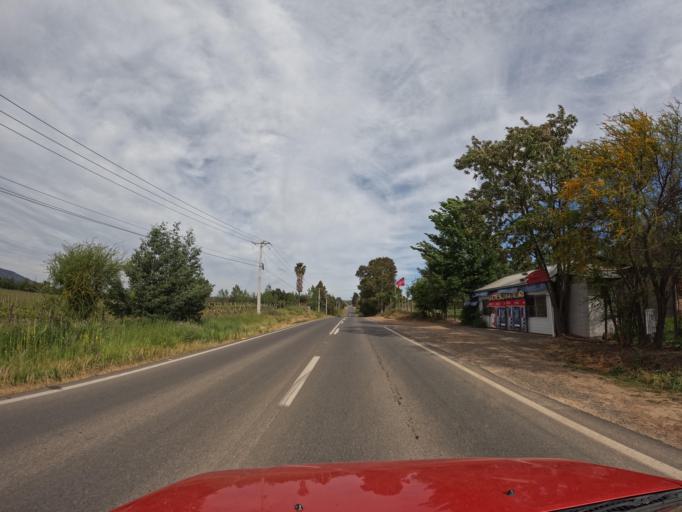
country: CL
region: Maule
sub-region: Provincia de Talca
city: Talca
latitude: -35.3868
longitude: -71.8180
